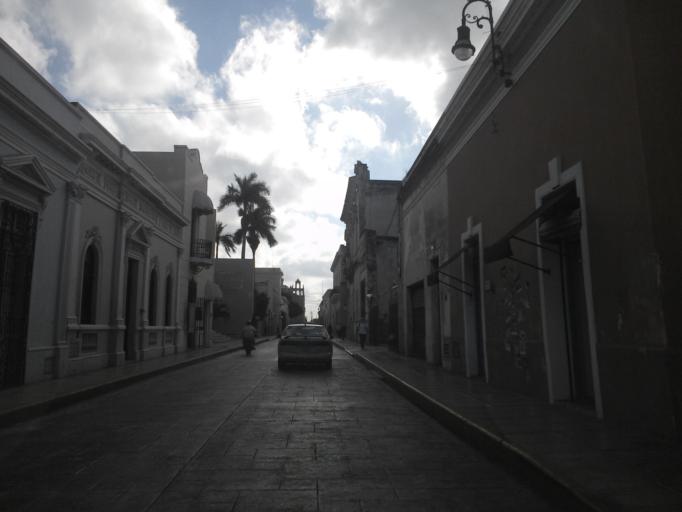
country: MX
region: Yucatan
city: Merida
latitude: 20.9680
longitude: -89.6184
